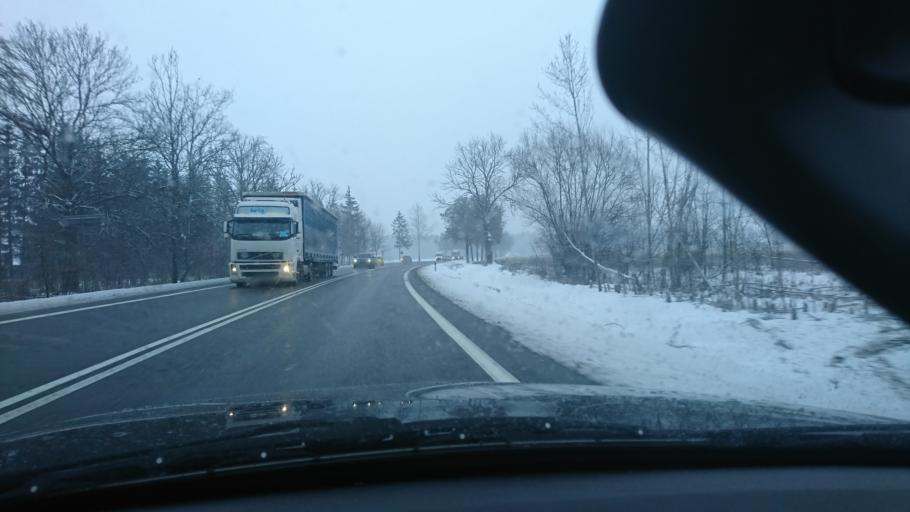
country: PL
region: Masovian Voivodeship
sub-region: Powiat ciechanowski
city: Glinojeck
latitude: 52.8273
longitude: 20.2594
